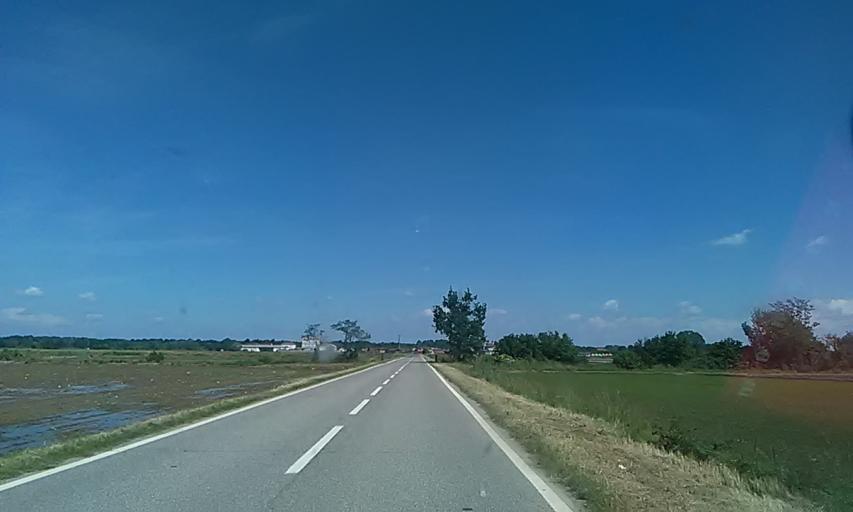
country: IT
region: Piedmont
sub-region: Provincia di Vercelli
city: Albano Vercellese
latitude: 45.4307
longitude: 8.3663
